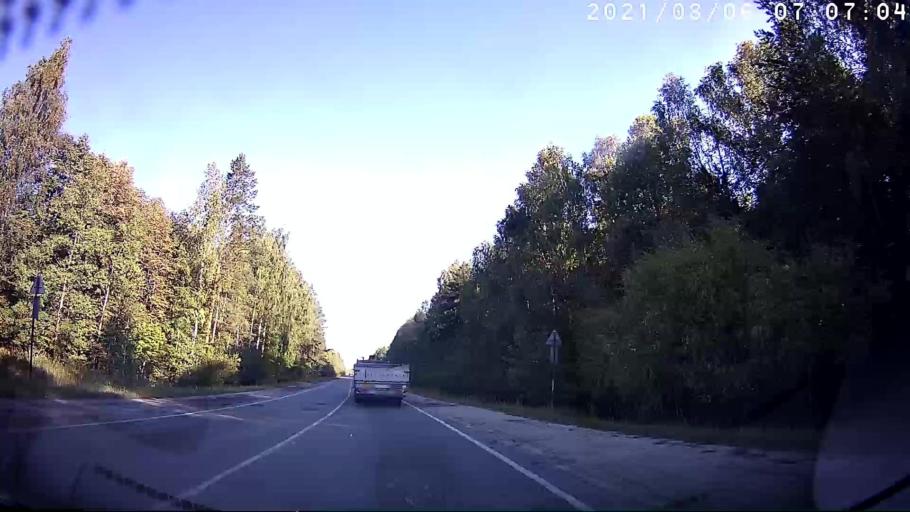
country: RU
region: Mariy-El
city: Yoshkar-Ola
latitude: 56.5613
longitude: 47.9807
